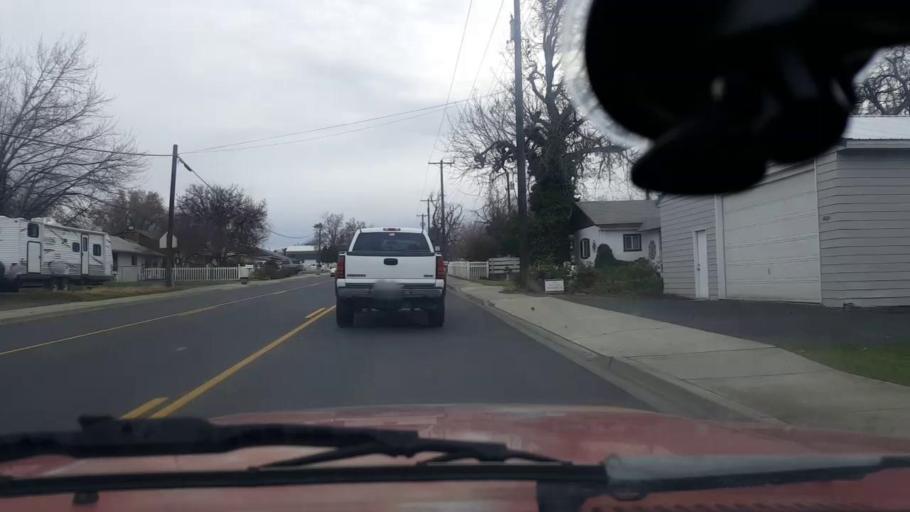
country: US
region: Washington
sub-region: Asotin County
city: West Clarkston-Highland
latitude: 46.4106
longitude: -117.0692
